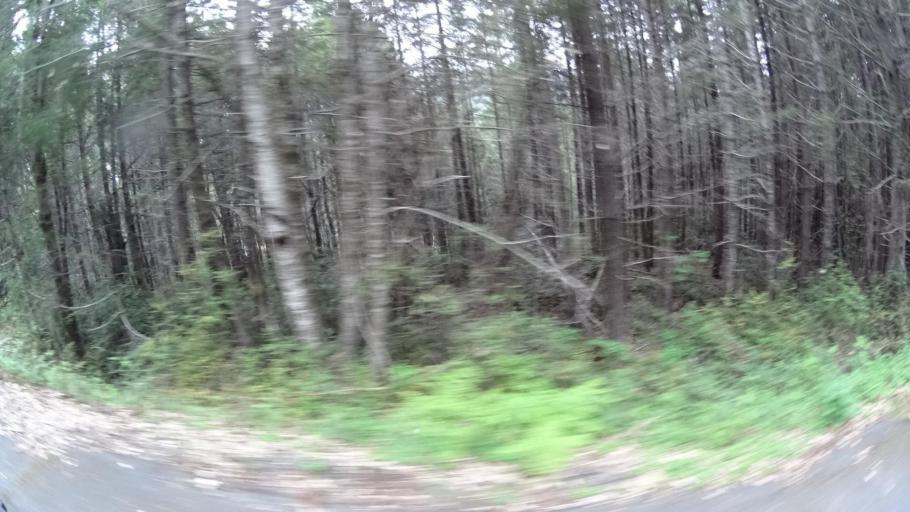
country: US
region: California
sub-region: Humboldt County
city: Willow Creek
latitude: 41.2015
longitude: -123.7614
